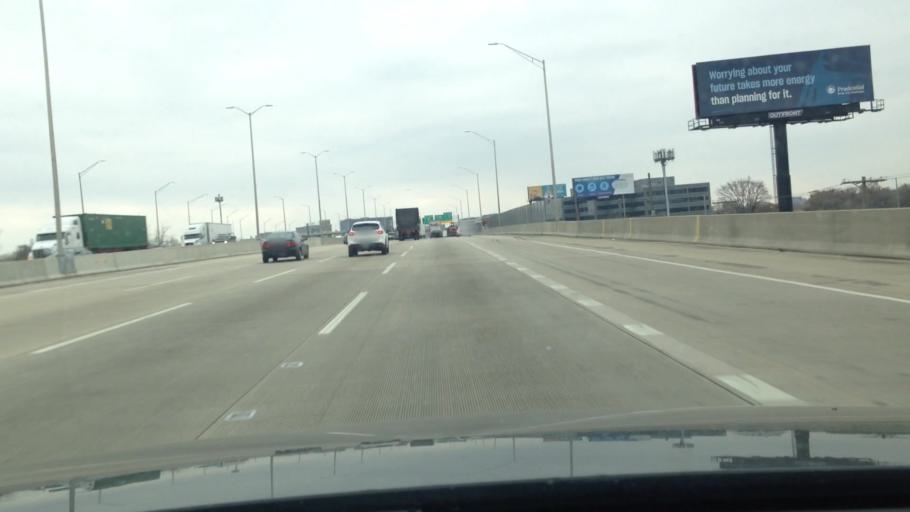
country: US
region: Illinois
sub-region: Cook County
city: Rosemont
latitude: 42.0003
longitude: -87.8833
